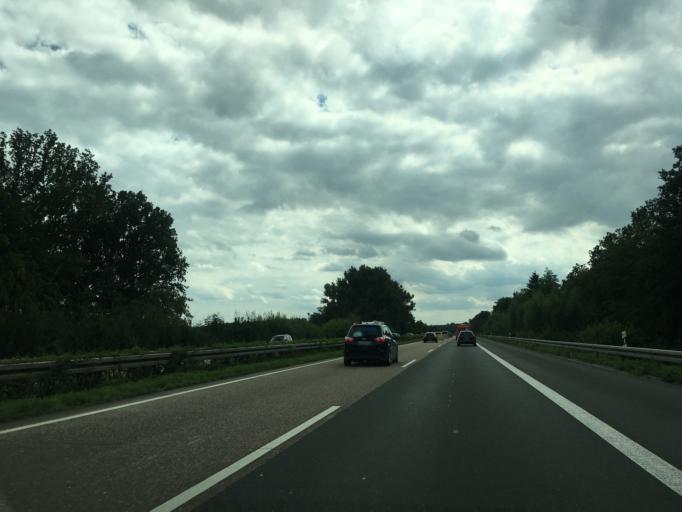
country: DE
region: North Rhine-Westphalia
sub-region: Regierungsbezirk Munster
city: Senden
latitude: 51.8738
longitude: 7.5761
